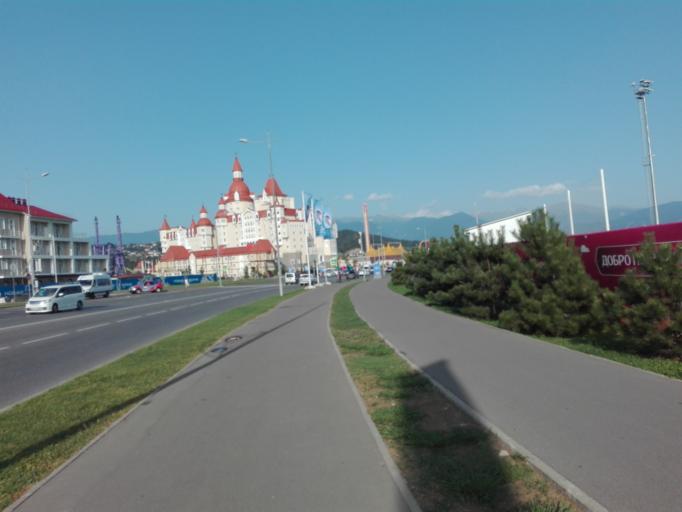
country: RU
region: Krasnodarskiy
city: Adler
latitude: 43.4020
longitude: 39.9604
